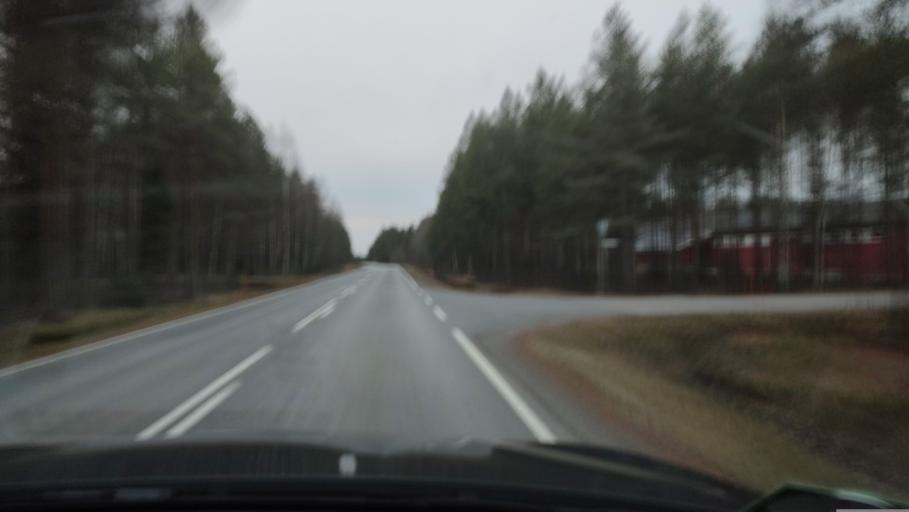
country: FI
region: Southern Ostrobothnia
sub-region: Suupohja
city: Karijoki
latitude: 62.3236
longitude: 21.7690
